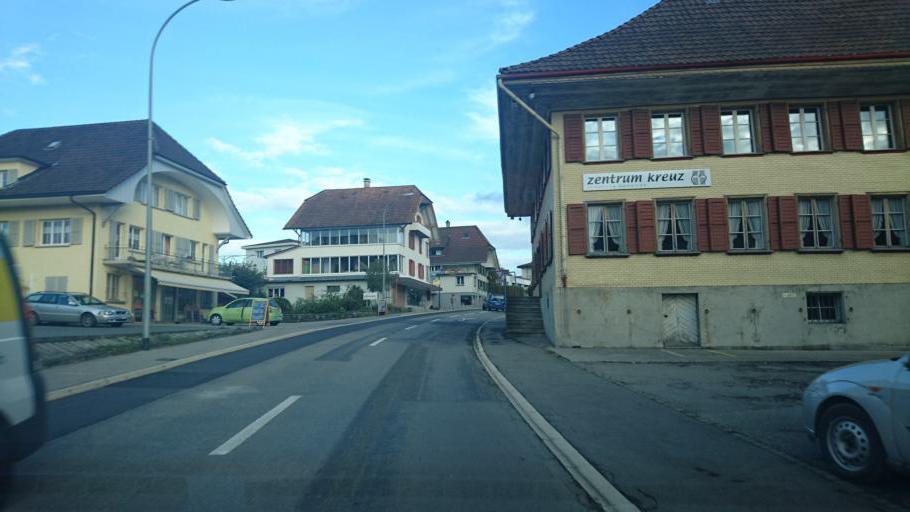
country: CH
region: Bern
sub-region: Bern-Mittelland District
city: Biglen
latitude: 46.9258
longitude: 7.6266
